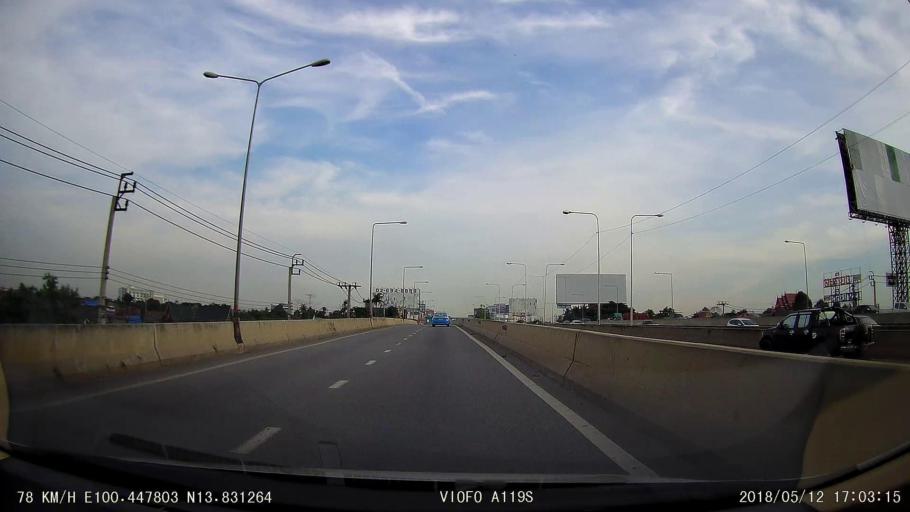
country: TH
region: Nonthaburi
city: Bang Kruai
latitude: 13.8307
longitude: 100.4479
